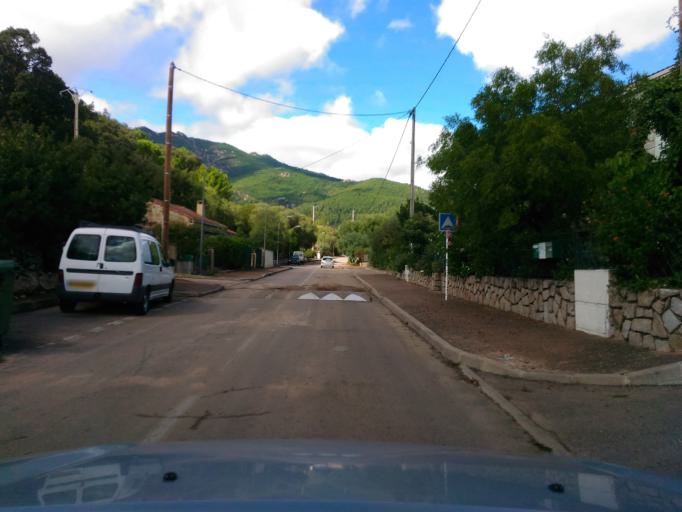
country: FR
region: Corsica
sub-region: Departement de la Corse-du-Sud
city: Porto-Vecchio
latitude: 41.7085
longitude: 9.3141
